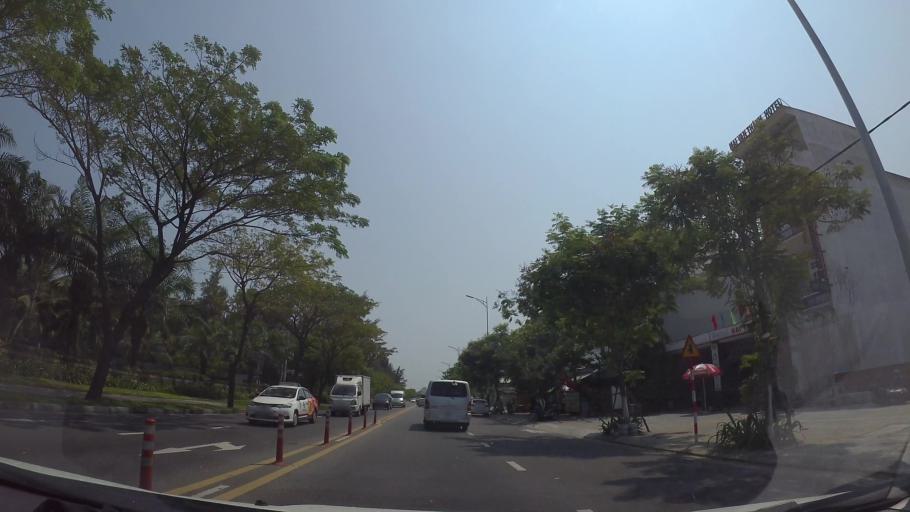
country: VN
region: Da Nang
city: Ngu Hanh Son
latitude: 15.9994
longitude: 108.2674
